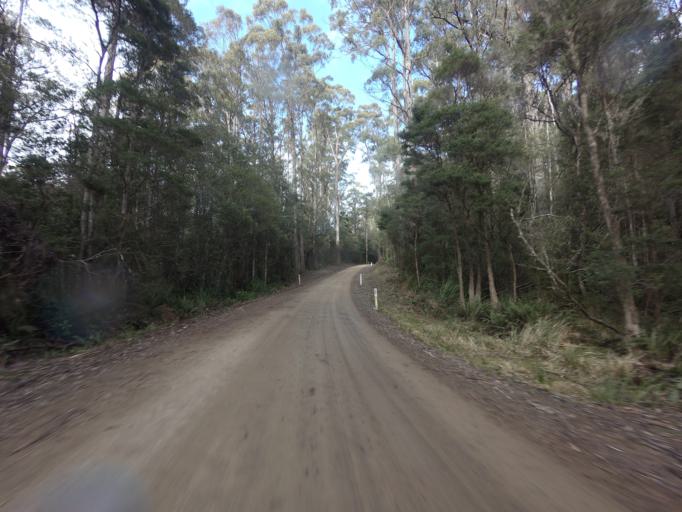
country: AU
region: Tasmania
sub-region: Huon Valley
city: Geeveston
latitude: -43.5713
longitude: 146.8912
